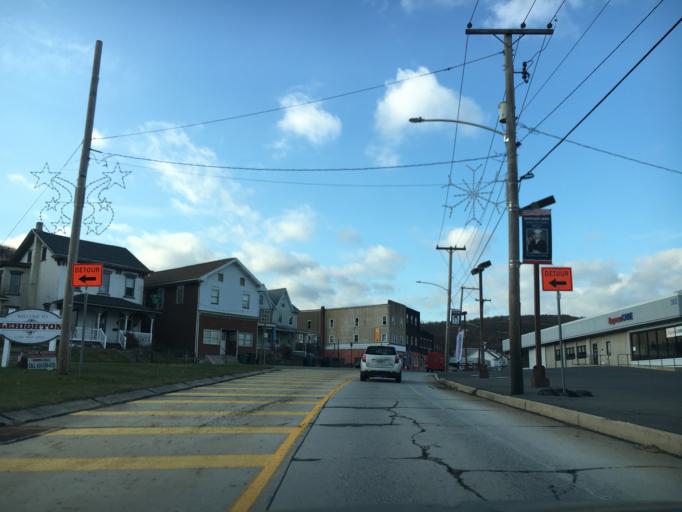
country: US
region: Pennsylvania
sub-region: Carbon County
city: Lehighton
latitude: 40.8380
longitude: -75.7089
